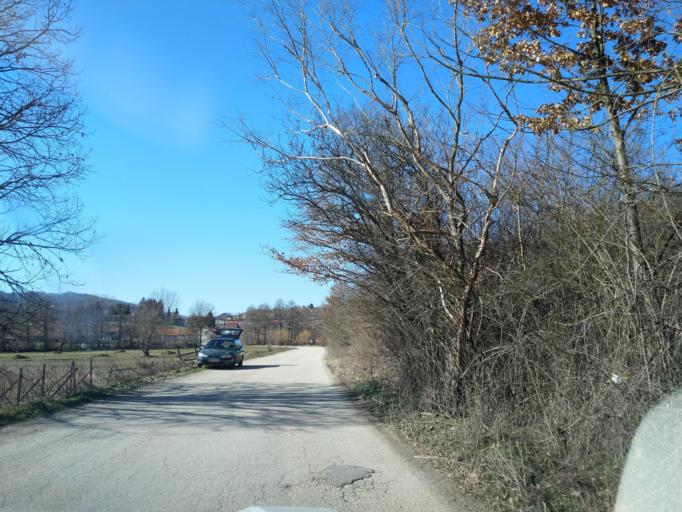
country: RS
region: Central Serbia
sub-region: Zlatiborski Okrug
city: Kosjeric
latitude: 43.9375
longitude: 19.8801
